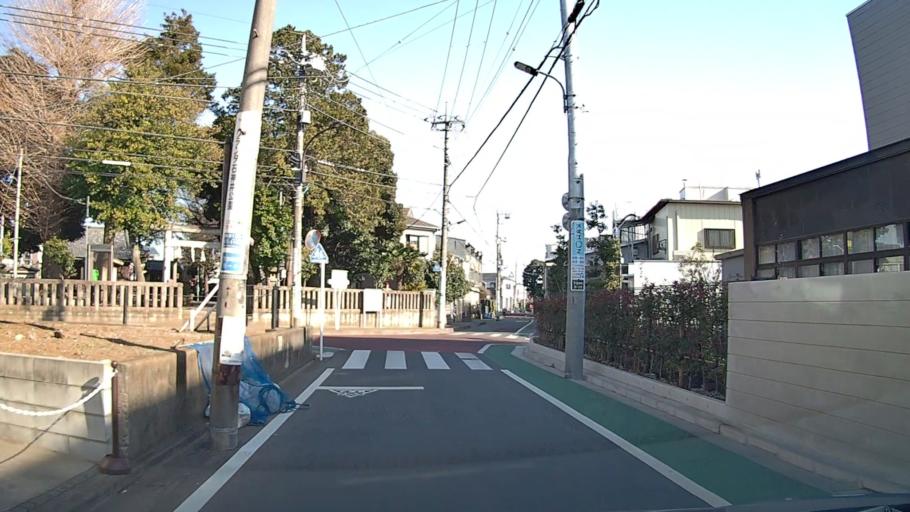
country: JP
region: Tokyo
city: Musashino
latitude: 35.7319
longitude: 139.6054
